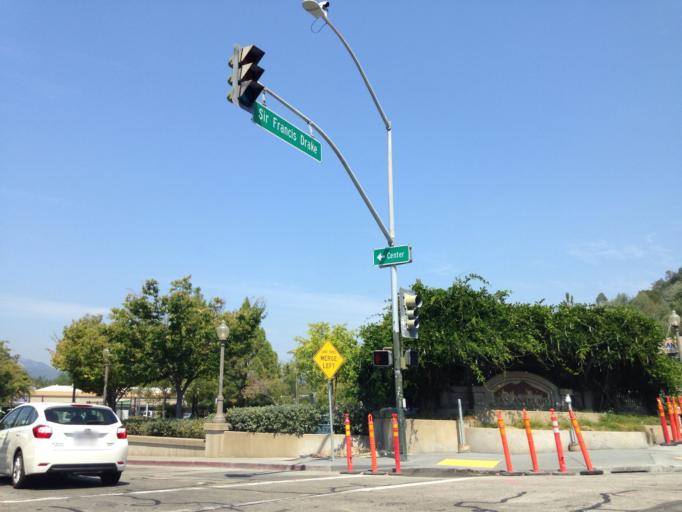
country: US
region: California
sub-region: Marin County
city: San Anselmo
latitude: 37.9765
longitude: -122.5616
